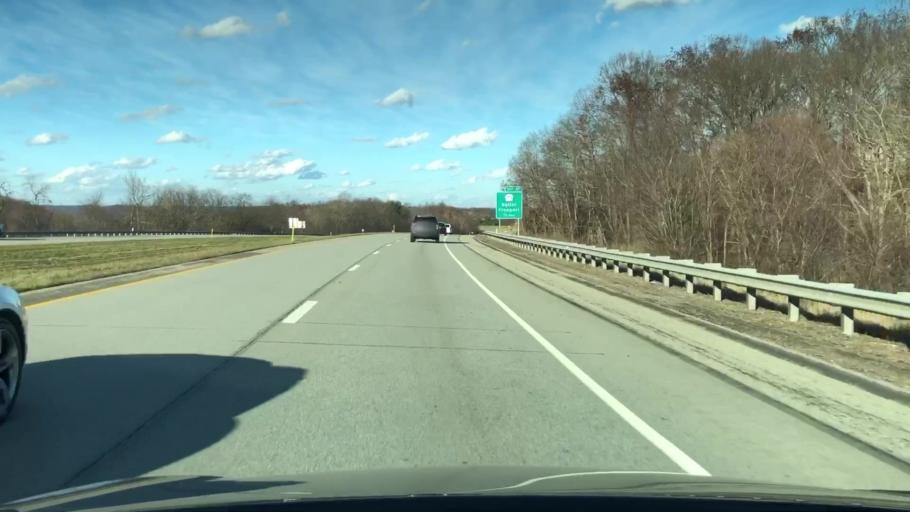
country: US
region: Pennsylvania
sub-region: Armstrong County
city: Freeport
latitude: 40.6818
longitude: -79.7139
